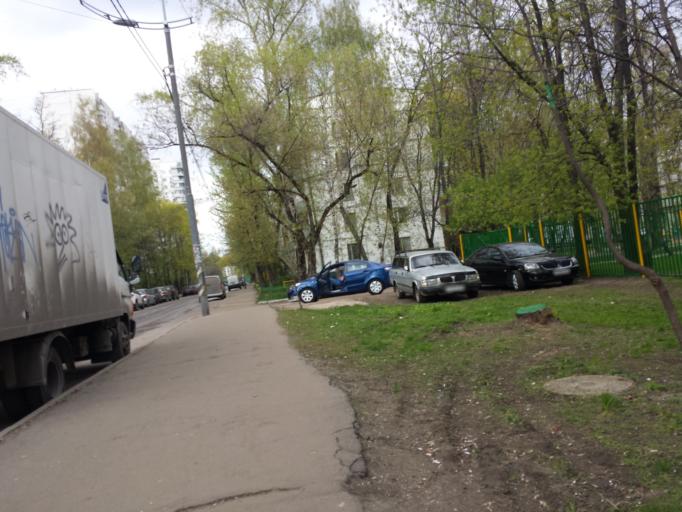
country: RU
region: Moskovskaya
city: Novogireyevo
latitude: 55.7550
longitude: 37.8260
